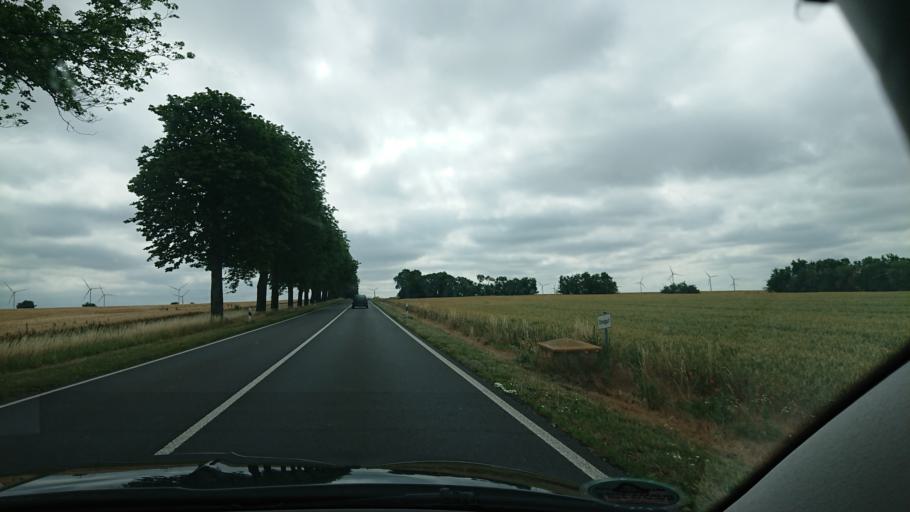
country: DE
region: Brandenburg
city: Plattenburg
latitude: 53.0006
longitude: 12.0677
